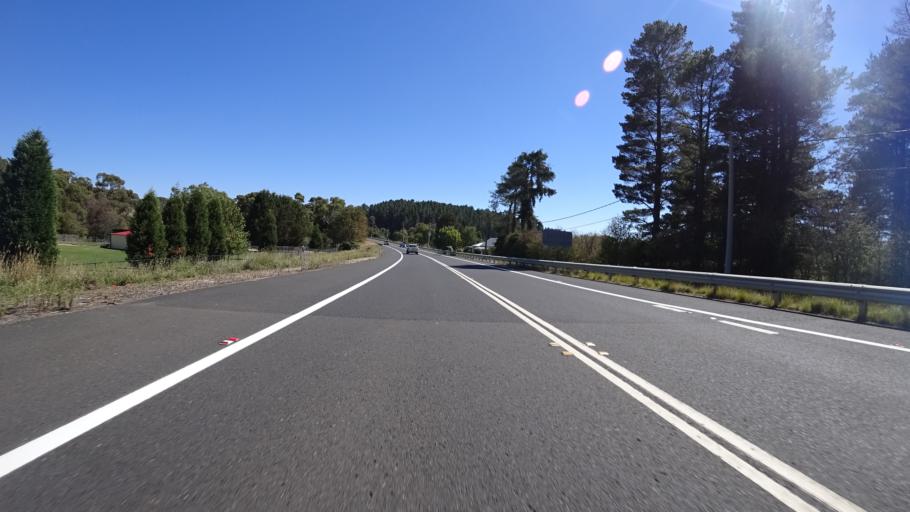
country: AU
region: New South Wales
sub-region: Lithgow
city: Portland
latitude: -33.3830
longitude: 150.0795
